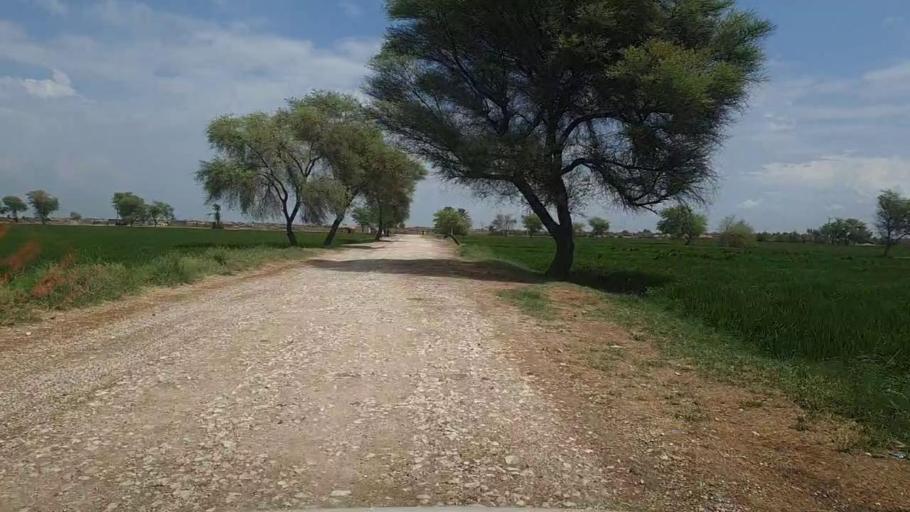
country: PK
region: Sindh
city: Kandhkot
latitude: 28.3421
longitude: 69.2199
